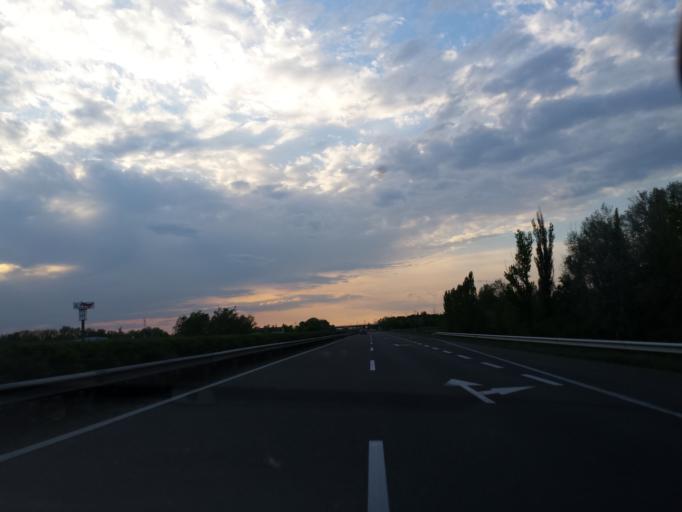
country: HU
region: Gyor-Moson-Sopron
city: Mosonszentmiklos
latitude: 47.7474
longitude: 17.4212
